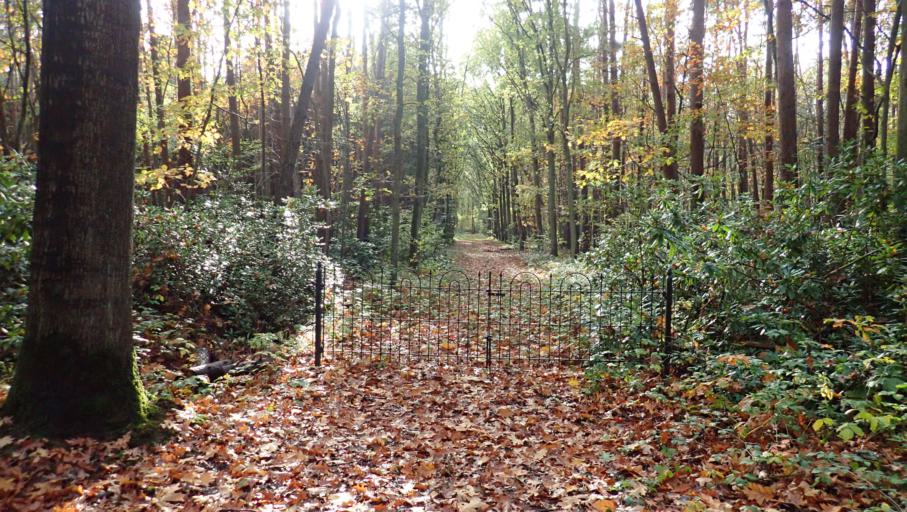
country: BE
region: Flanders
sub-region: Provincie Antwerpen
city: Zoersel
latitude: 51.2639
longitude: 4.6924
